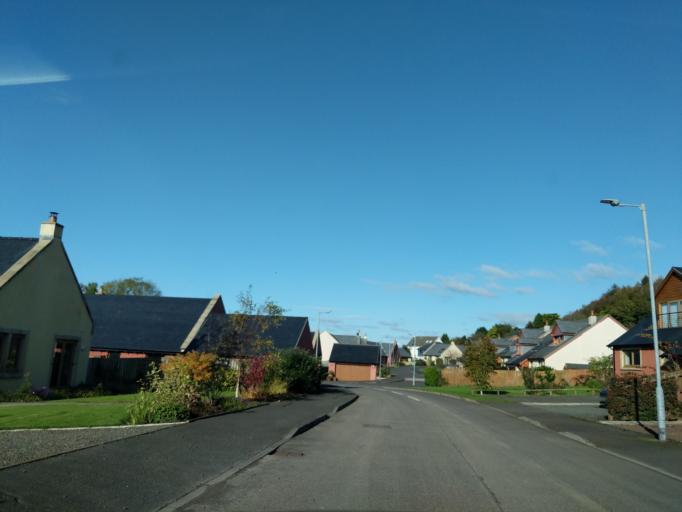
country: GB
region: Scotland
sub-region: Dumfries and Galloway
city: Kirkcudbright
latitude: 54.8293
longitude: -4.0508
